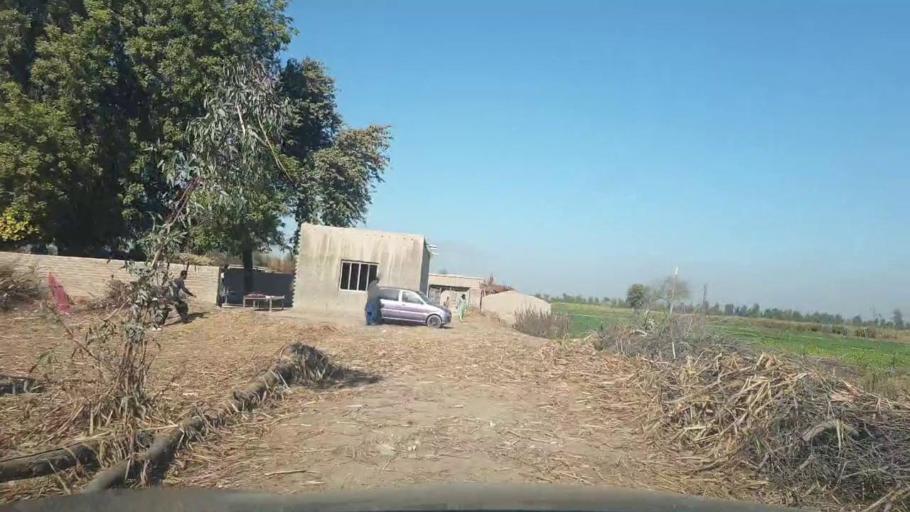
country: PK
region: Sindh
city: Mirpur Mathelo
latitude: 28.0643
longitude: 69.4942
